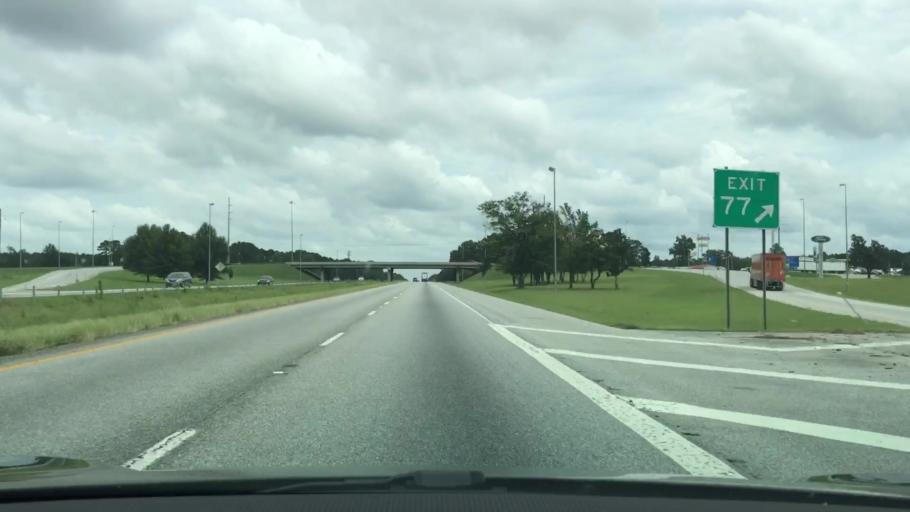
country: US
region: Alabama
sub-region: Chambers County
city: Huguley
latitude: 32.8193
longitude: -85.2154
